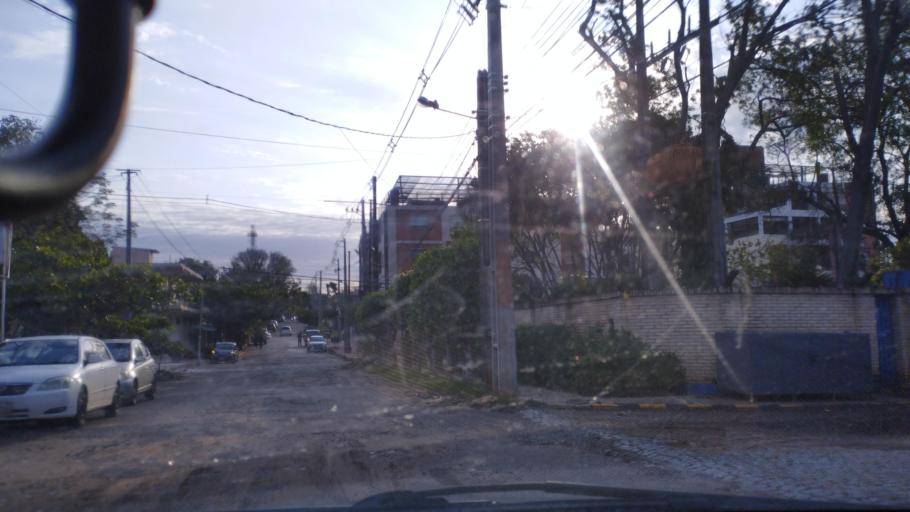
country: PY
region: Central
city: Fernando de la Mora
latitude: -25.3087
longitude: -57.5328
